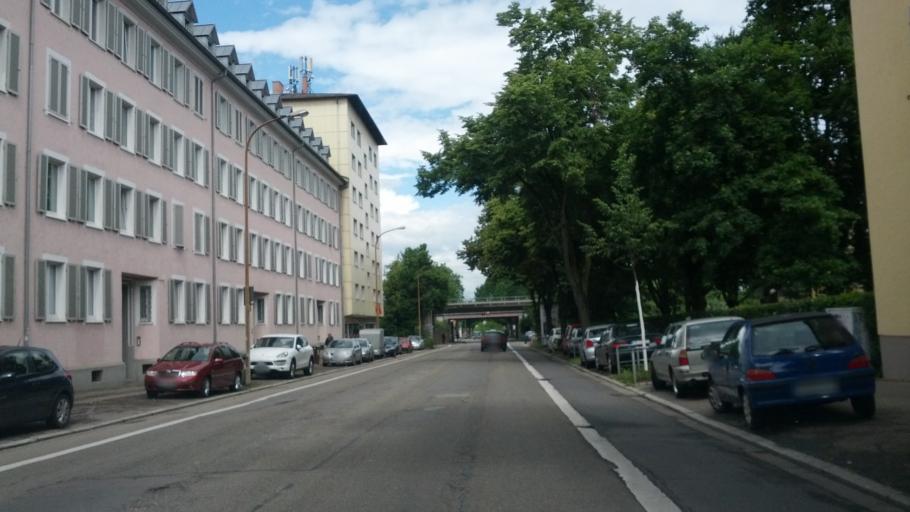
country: DE
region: Baden-Wuerttemberg
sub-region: Freiburg Region
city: Freiburg
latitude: 48.0200
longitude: 7.8543
